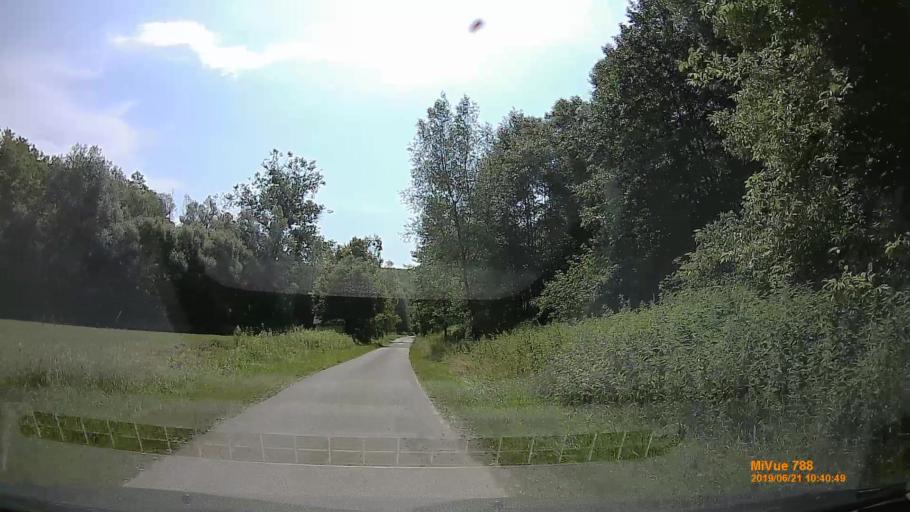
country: HU
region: Baranya
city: Buekkoesd
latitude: 46.1354
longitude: 17.9993
